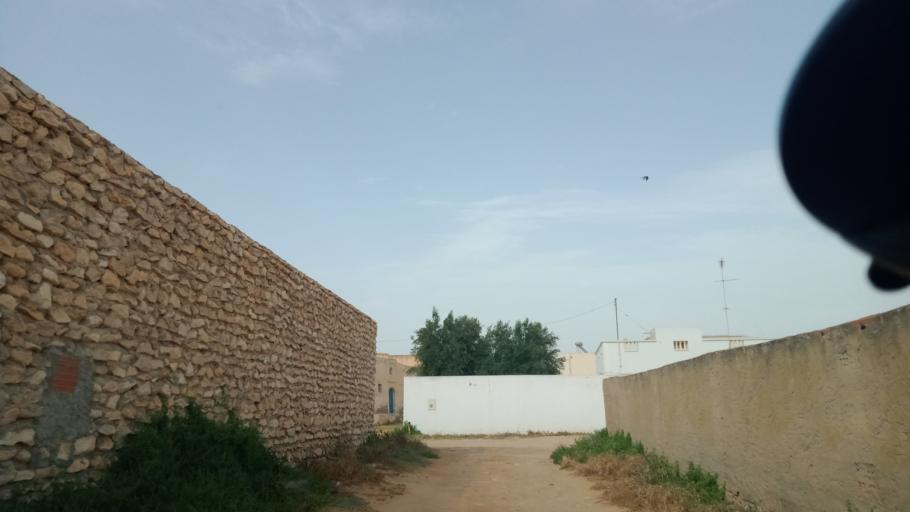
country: TN
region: Safaqis
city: Al Qarmadah
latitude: 34.7836
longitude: 10.7628
